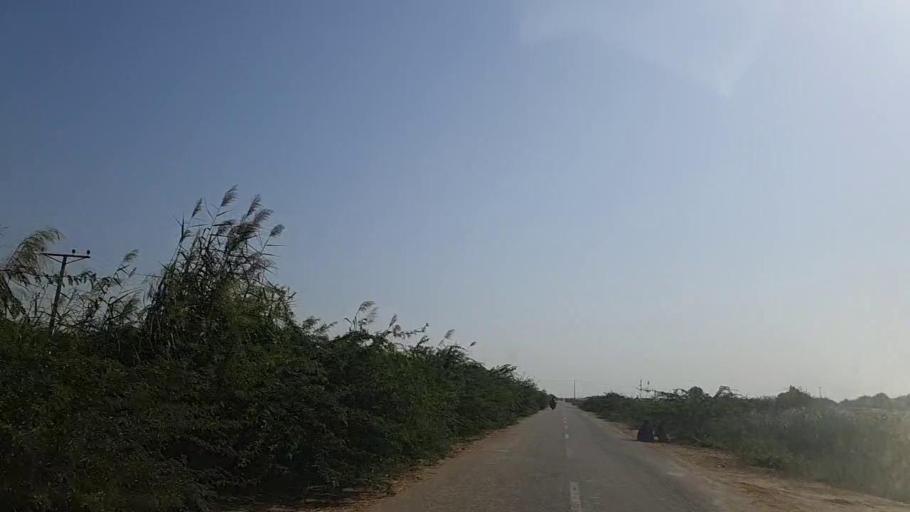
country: PK
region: Sindh
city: Jati
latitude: 24.5128
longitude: 68.2746
